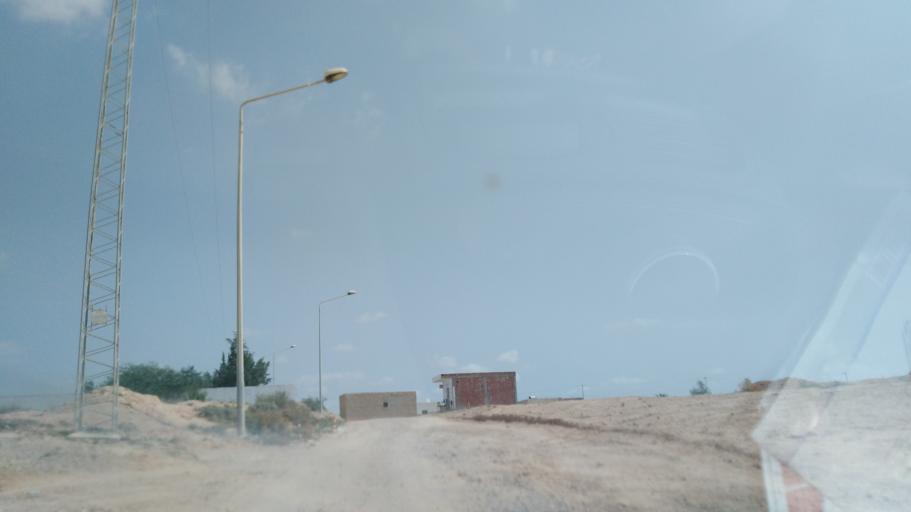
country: TN
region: Safaqis
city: Sfax
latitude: 34.6403
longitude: 10.6167
